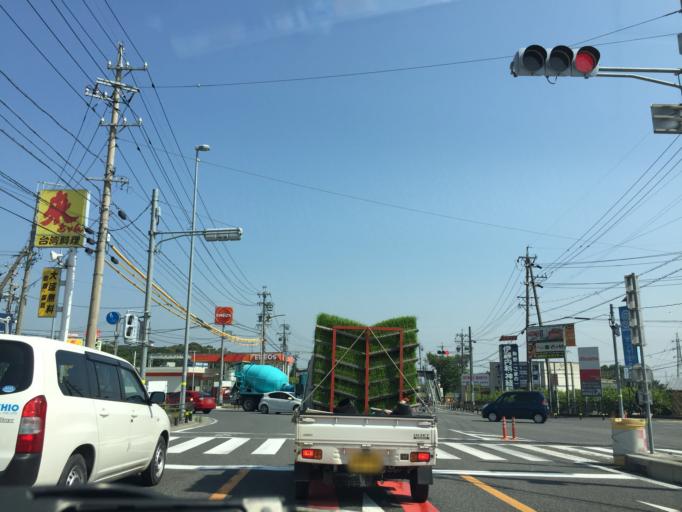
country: JP
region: Aichi
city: Sobue
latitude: 35.2245
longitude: 136.5962
